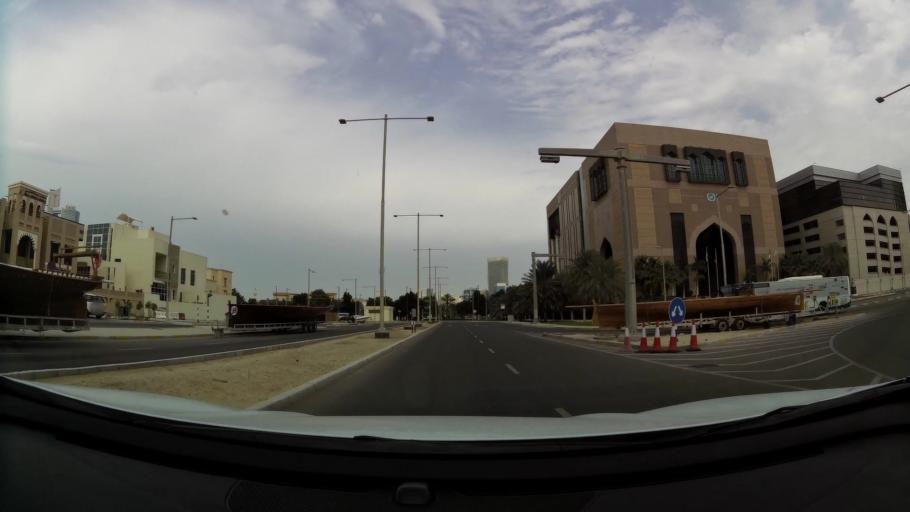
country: AE
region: Abu Dhabi
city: Abu Dhabi
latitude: 24.4561
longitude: 54.3350
